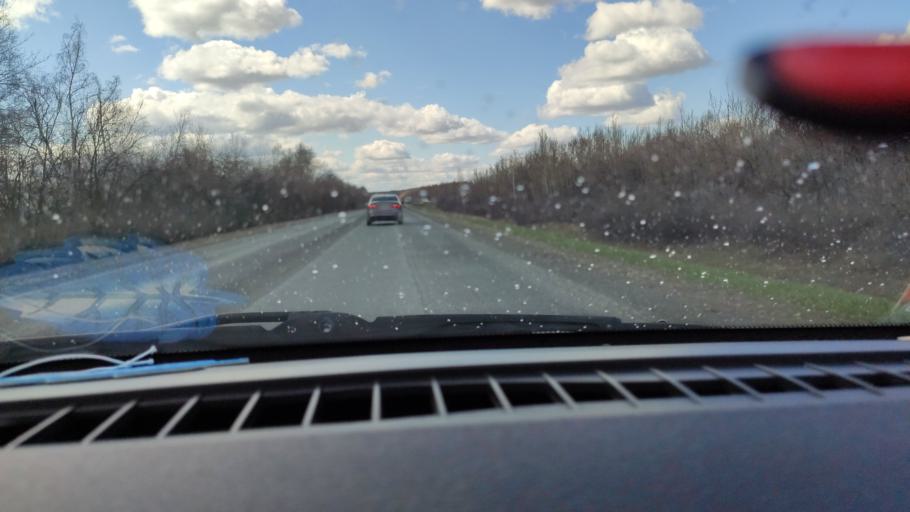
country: RU
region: Saratov
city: Dukhovnitskoye
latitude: 52.6629
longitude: 48.2130
